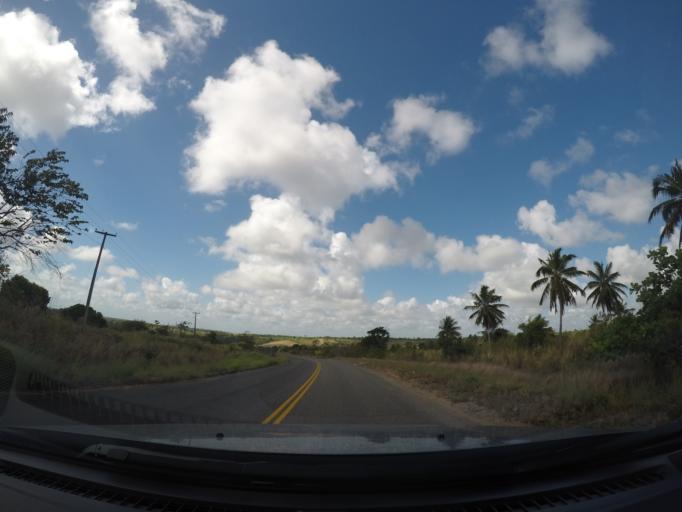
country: BR
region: Paraiba
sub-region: Pitimbu
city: Pitimbu
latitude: -7.4136
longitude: -34.8251
